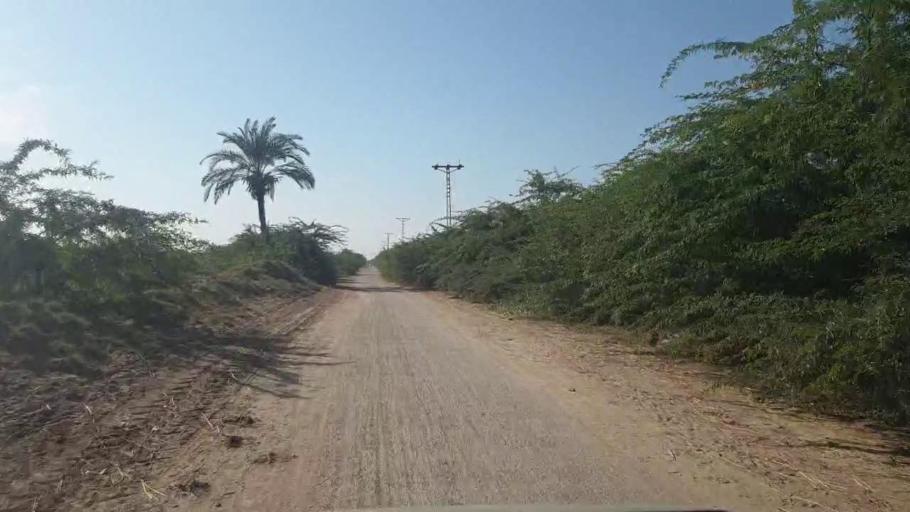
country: PK
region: Sindh
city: Rajo Khanani
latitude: 24.9516
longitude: 68.7945
